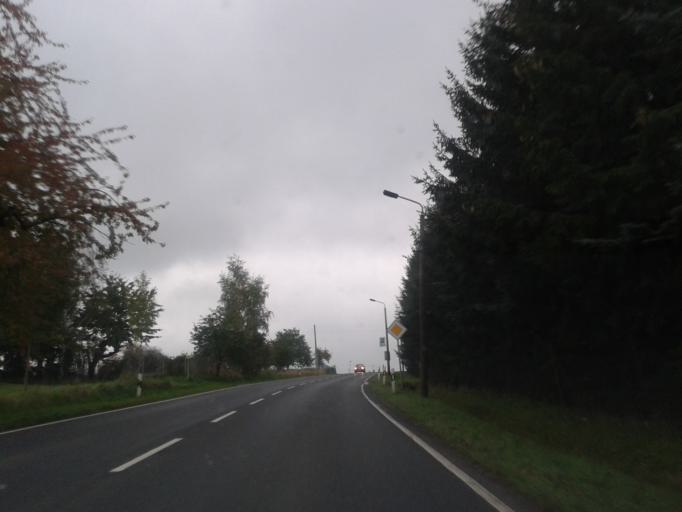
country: DE
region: Saxony
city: Wilsdruff
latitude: 51.0542
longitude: 13.5424
